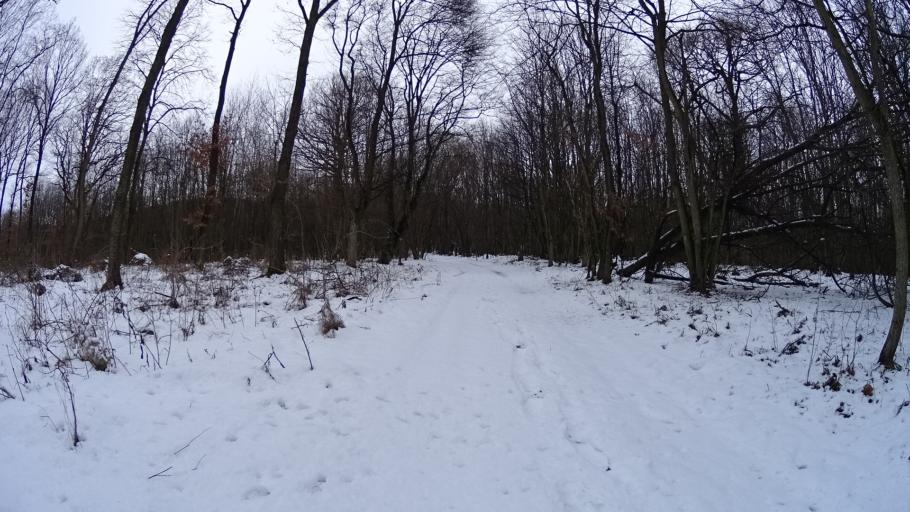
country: AT
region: Lower Austria
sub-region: Politischer Bezirk Korneuburg
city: Niederhollabrunn
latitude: 48.4185
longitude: 16.2972
